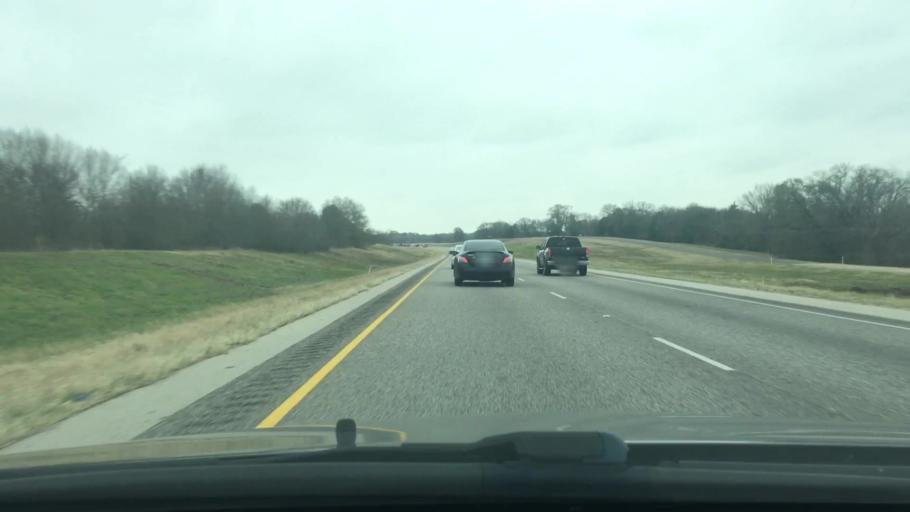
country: US
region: Texas
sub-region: Freestone County
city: Fairfield
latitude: 31.7942
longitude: -96.2520
